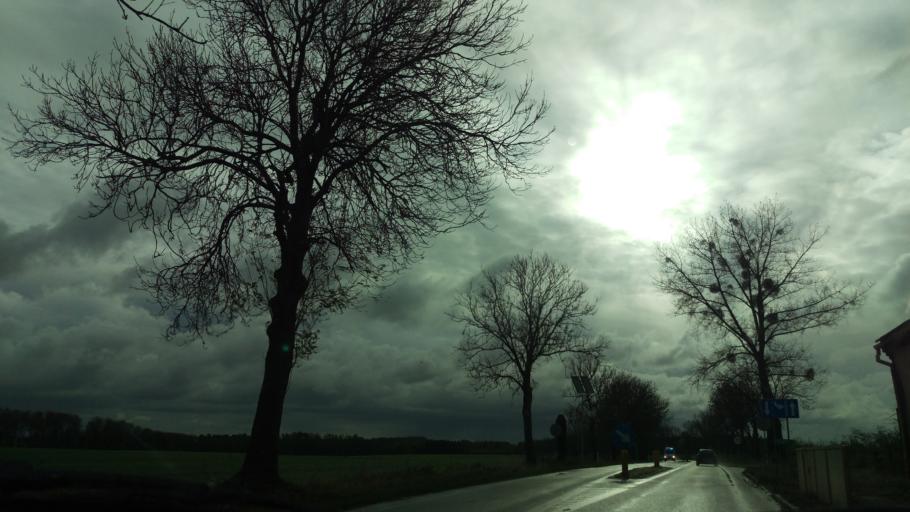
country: PL
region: West Pomeranian Voivodeship
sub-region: Powiat gryficki
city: Gryfice
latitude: 53.8700
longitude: 15.2164
